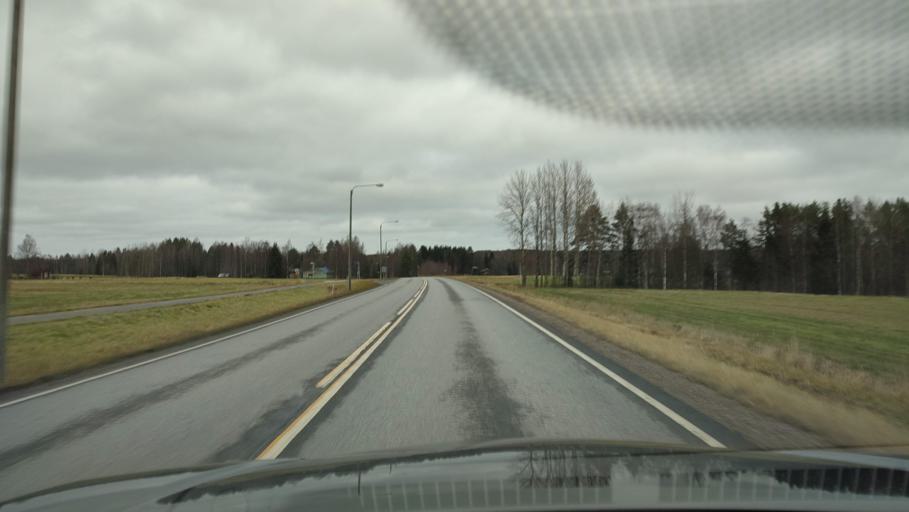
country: FI
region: Southern Ostrobothnia
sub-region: Seinaejoki
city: Kurikka
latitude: 62.5874
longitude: 22.4074
